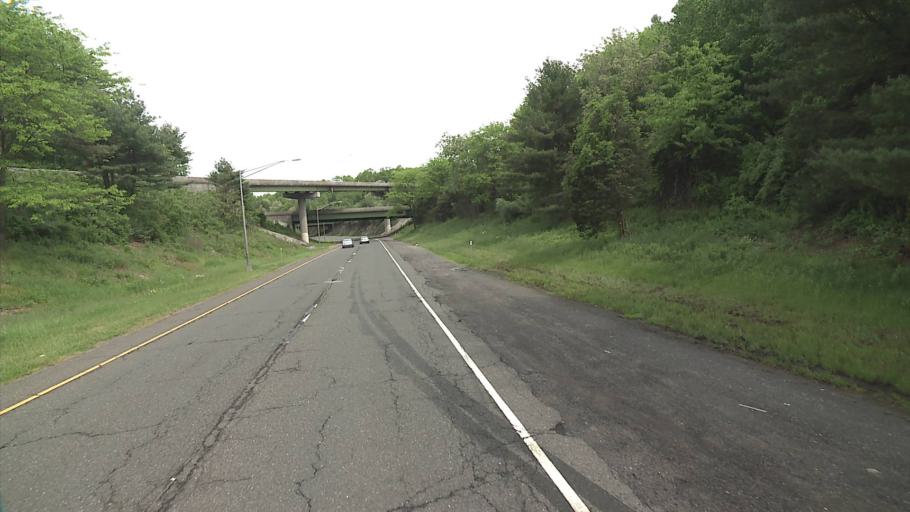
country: US
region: Connecticut
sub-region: Fairfield County
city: Newtown
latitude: 41.4127
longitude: -73.2677
